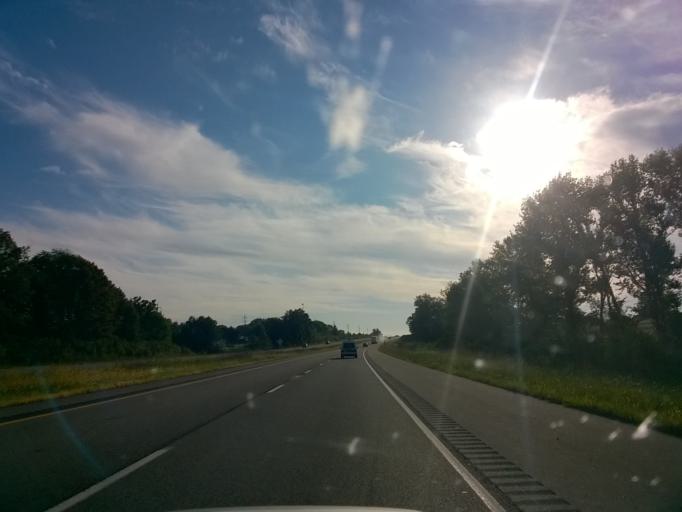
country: US
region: Indiana
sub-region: Warrick County
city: Boonville
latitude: 38.1994
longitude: -87.2734
